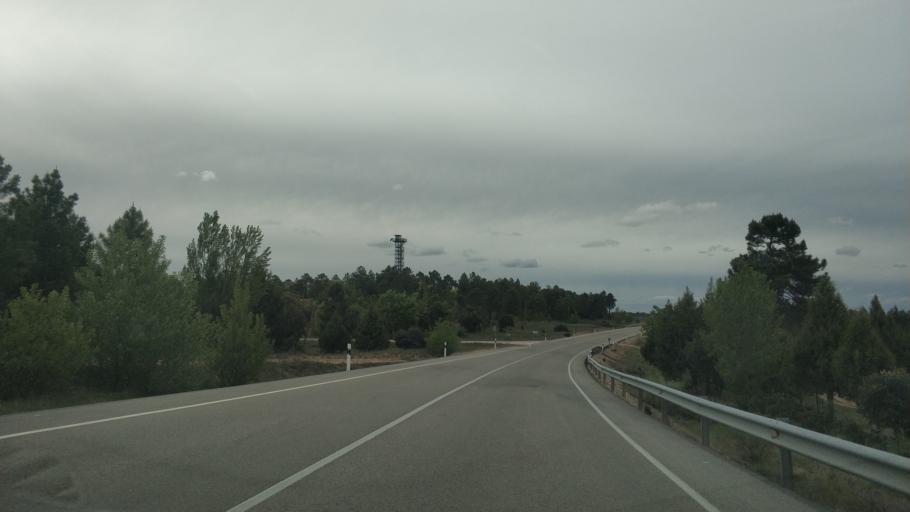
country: ES
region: Castille and Leon
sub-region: Provincia de Soria
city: Quintanas de Gormaz
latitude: 41.5321
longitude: -2.9489
